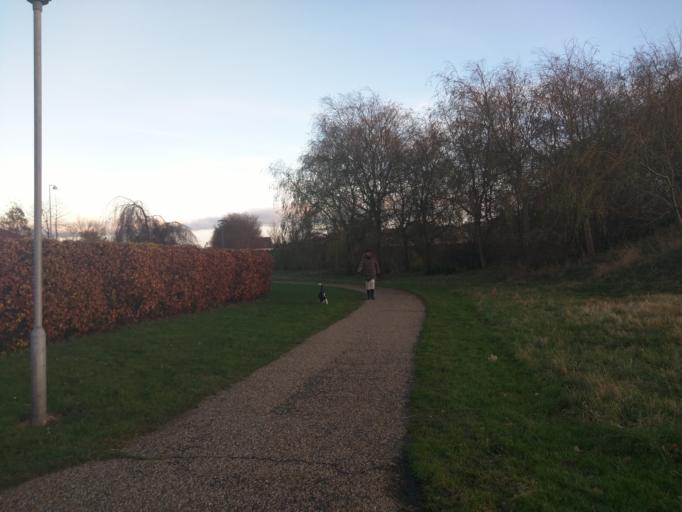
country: DK
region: Central Jutland
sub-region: Skanderborg Kommune
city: Horning
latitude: 56.0846
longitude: 10.0216
